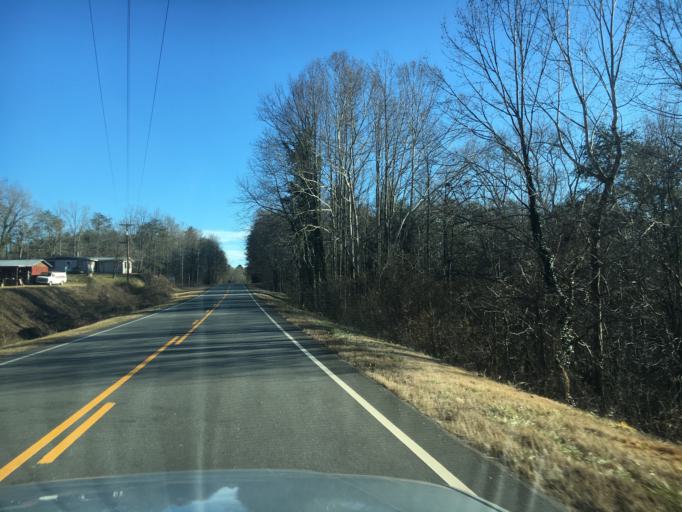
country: US
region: Georgia
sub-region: White County
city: Cleveland
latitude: 34.6659
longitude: -83.8573
